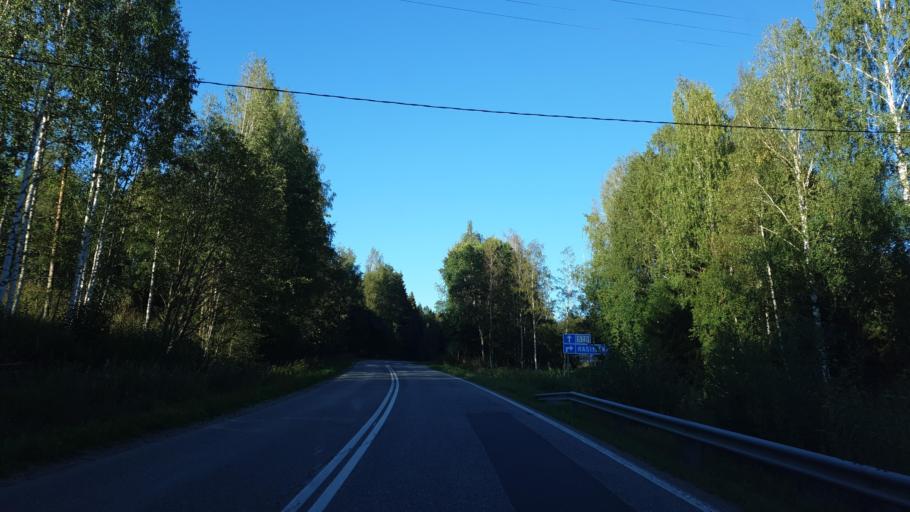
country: FI
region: Northern Savo
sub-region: Koillis-Savo
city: Juankoski
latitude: 63.0962
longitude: 28.4253
